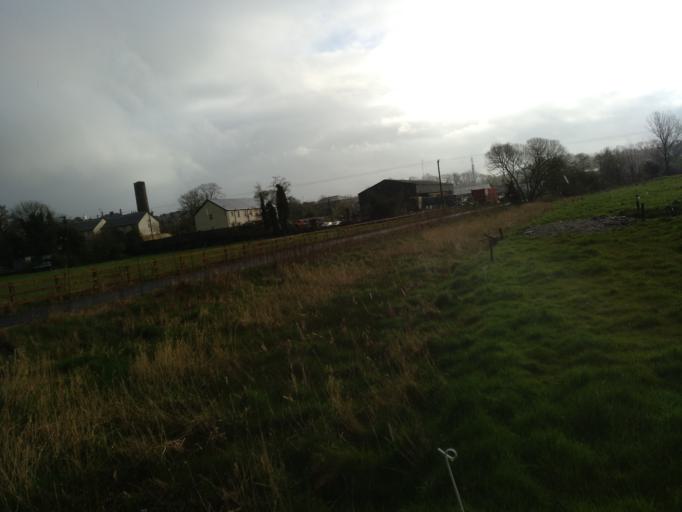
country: IE
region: Ulster
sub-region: County Monaghan
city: Clones
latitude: 54.1759
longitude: -7.2350
